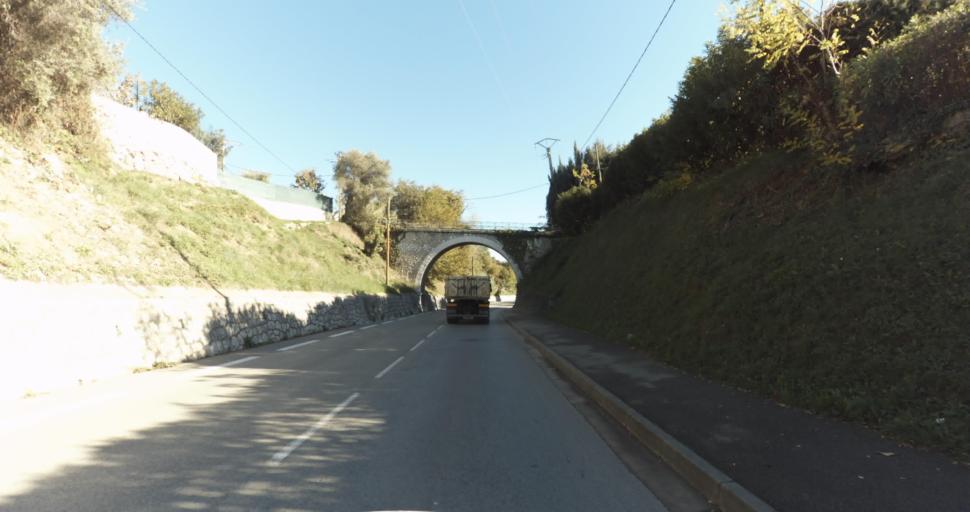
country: FR
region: Provence-Alpes-Cote d'Azur
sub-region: Departement des Alpes-Maritimes
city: Vence
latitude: 43.7249
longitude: 7.0921
